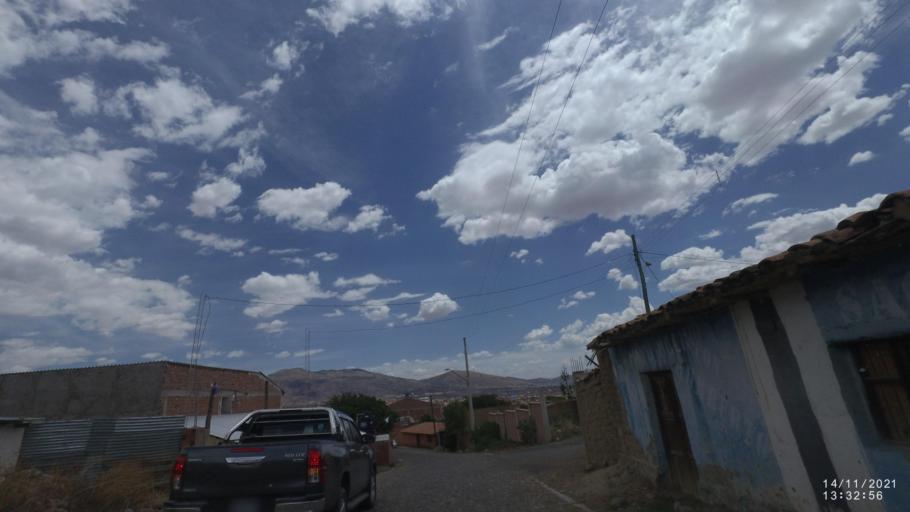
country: BO
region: Cochabamba
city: Colomi
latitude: -17.3977
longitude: -65.9850
